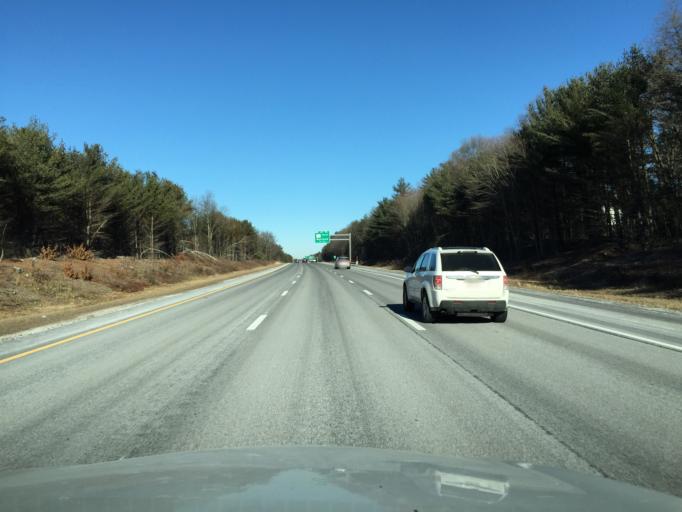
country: US
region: Massachusetts
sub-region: Bristol County
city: Mansfield
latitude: 42.0342
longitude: -71.2482
